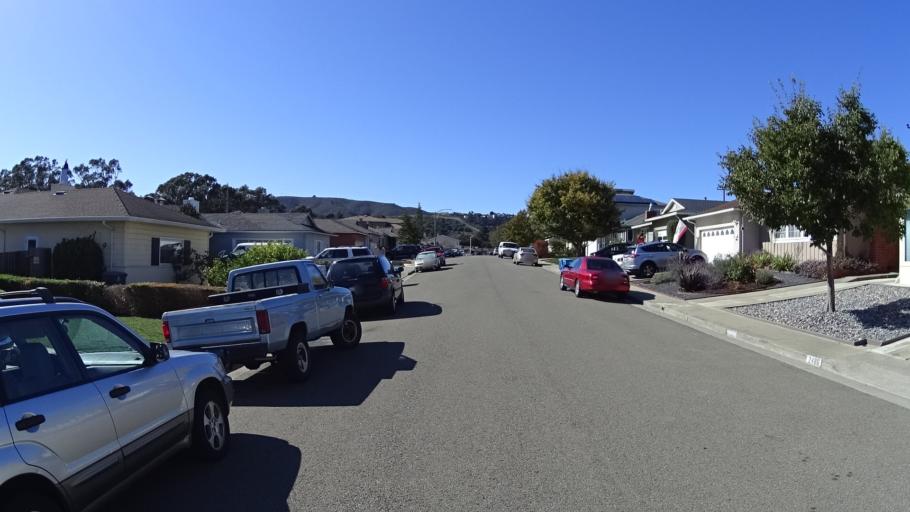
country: US
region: California
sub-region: San Mateo County
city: San Bruno
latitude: 37.6200
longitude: -122.4342
